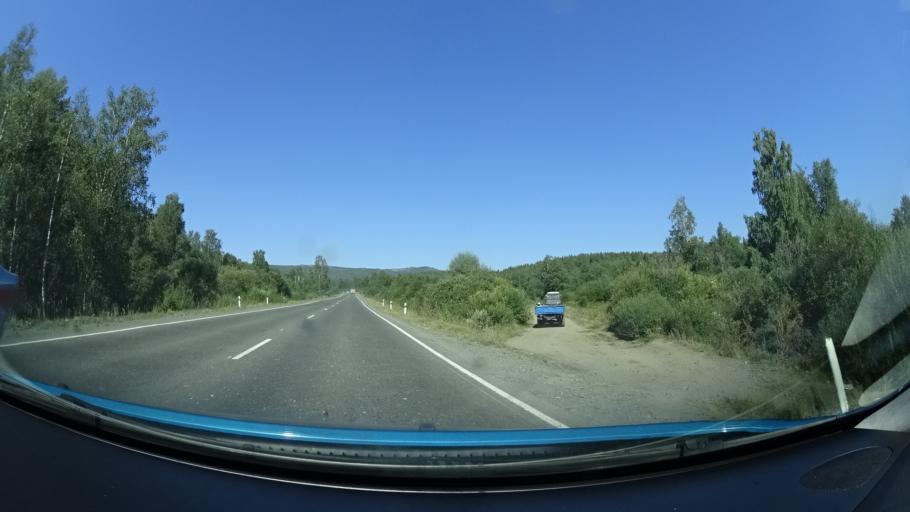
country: RU
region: Bashkortostan
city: Abzakovo
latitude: 53.8580
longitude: 58.5622
